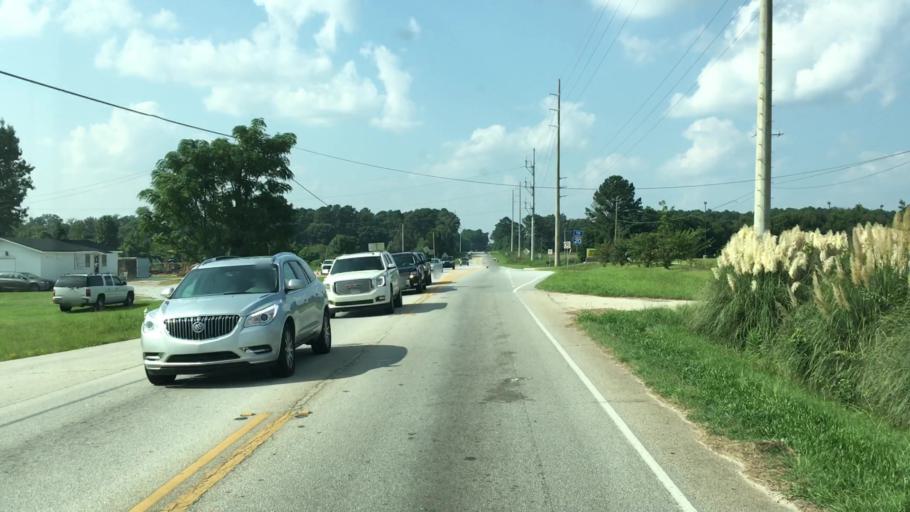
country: US
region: Georgia
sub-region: Walton County
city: Social Circle
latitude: 33.6005
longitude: -83.7506
